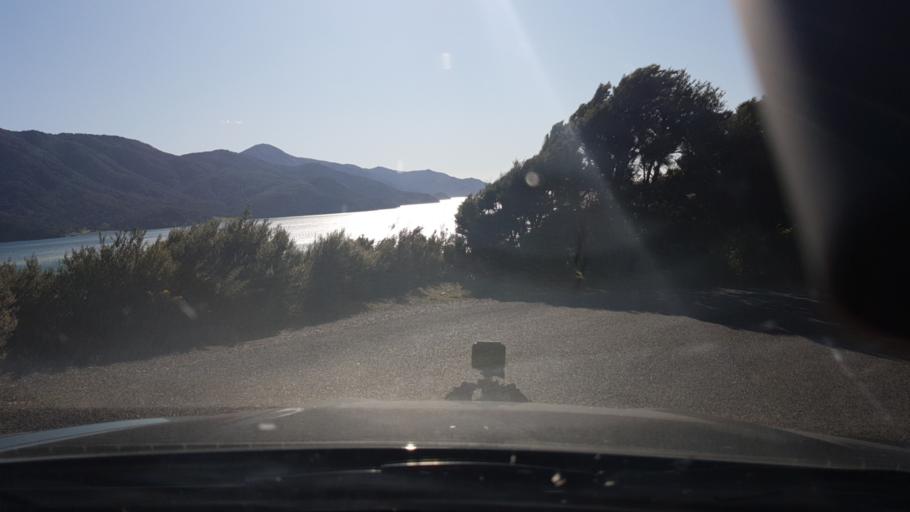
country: NZ
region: Marlborough
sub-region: Marlborough District
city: Picton
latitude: -40.9254
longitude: 173.8398
